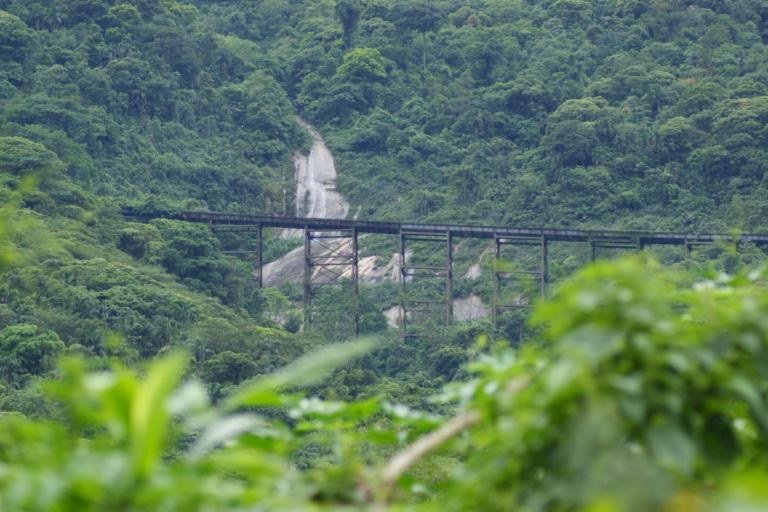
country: BR
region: Sao Paulo
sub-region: Rio Grande Da Serra
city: Rio Grande da Serra
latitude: -23.8218
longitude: -46.3607
